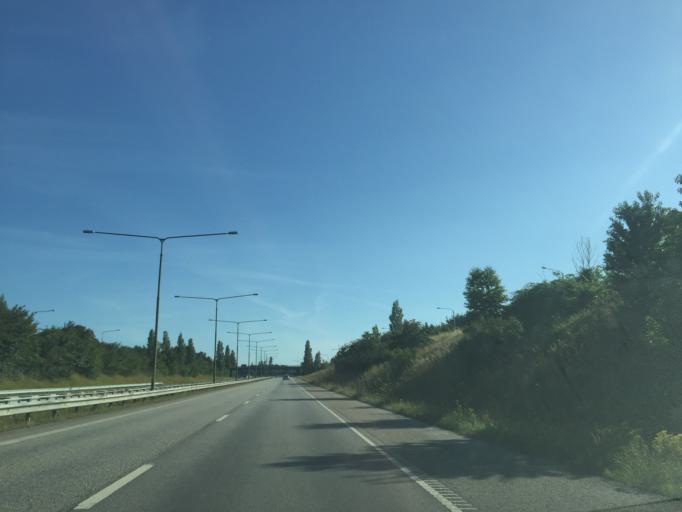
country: SE
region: Skane
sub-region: Malmo
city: Malmoe
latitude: 55.5640
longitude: 13.0013
